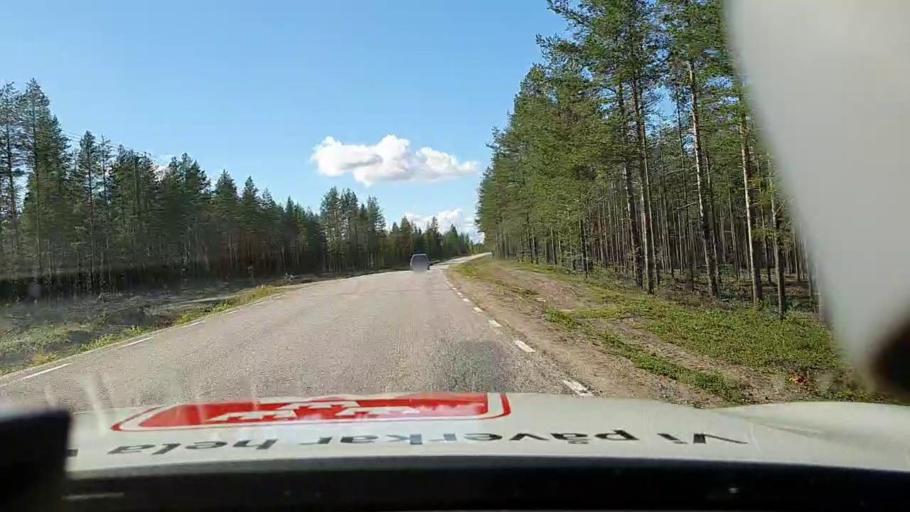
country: SE
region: Norrbotten
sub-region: Overkalix Kommun
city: OEverkalix
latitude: 66.2503
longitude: 22.8810
